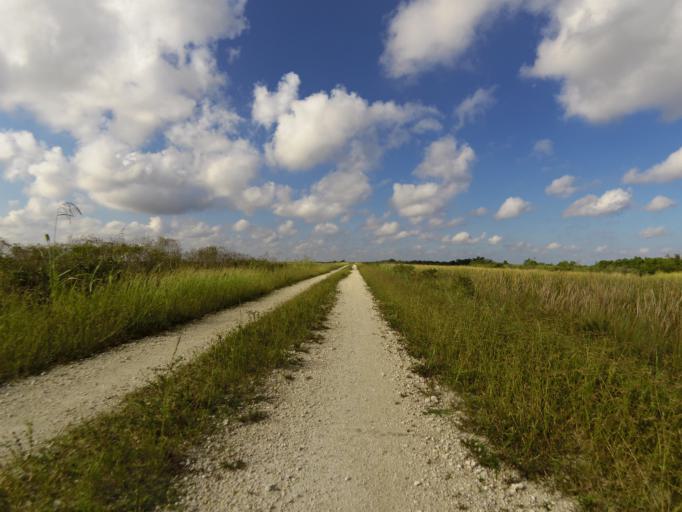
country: US
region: Florida
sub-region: Broward County
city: Weston
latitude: 26.0547
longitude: -80.4613
